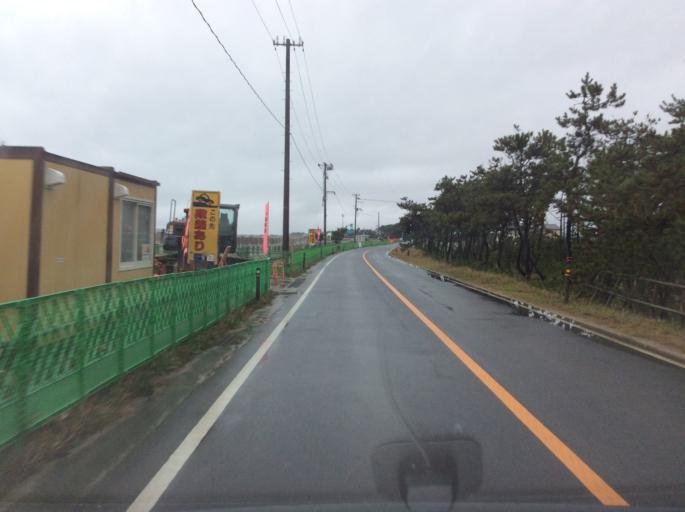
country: JP
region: Fukushima
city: Iwaki
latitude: 37.0924
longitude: 140.9838
